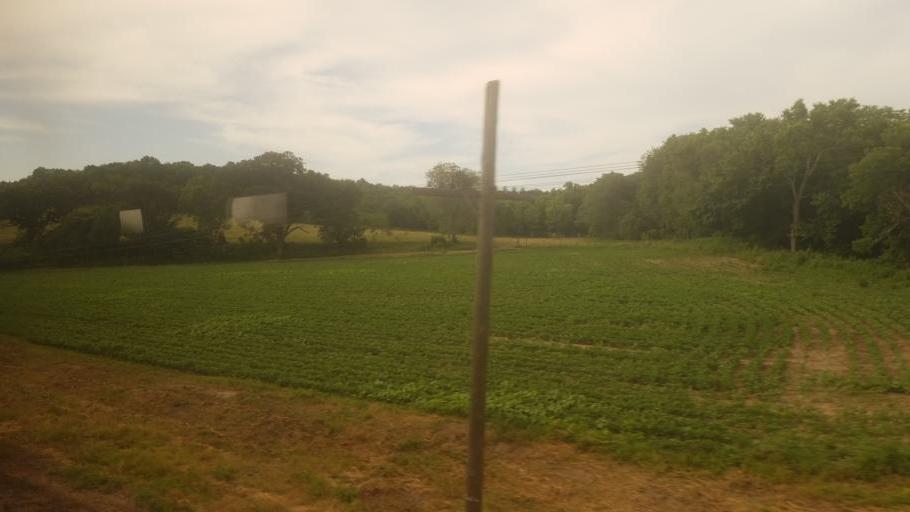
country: US
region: Kansas
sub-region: Jefferson County
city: Oskaloosa
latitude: 39.0602
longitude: -95.4231
